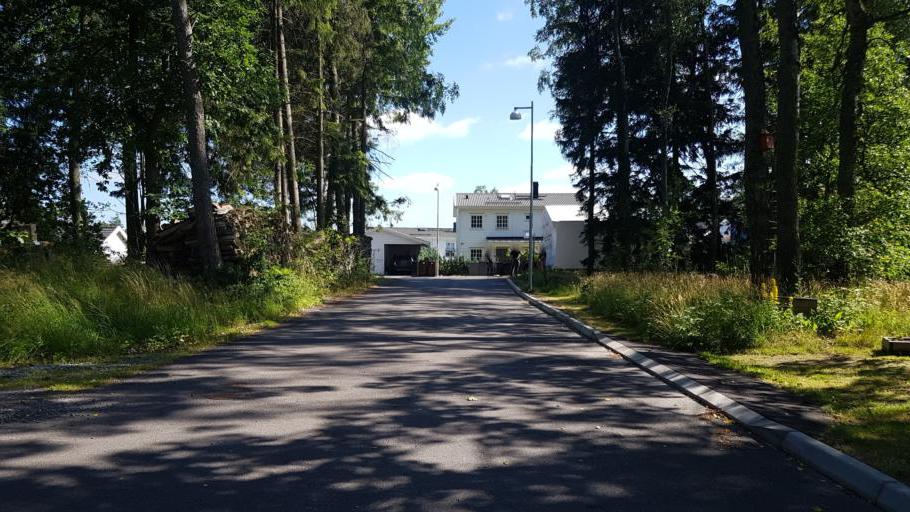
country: SE
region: Vaestra Goetaland
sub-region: Partille Kommun
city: Ojersjo
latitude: 57.6842
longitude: 12.0955
